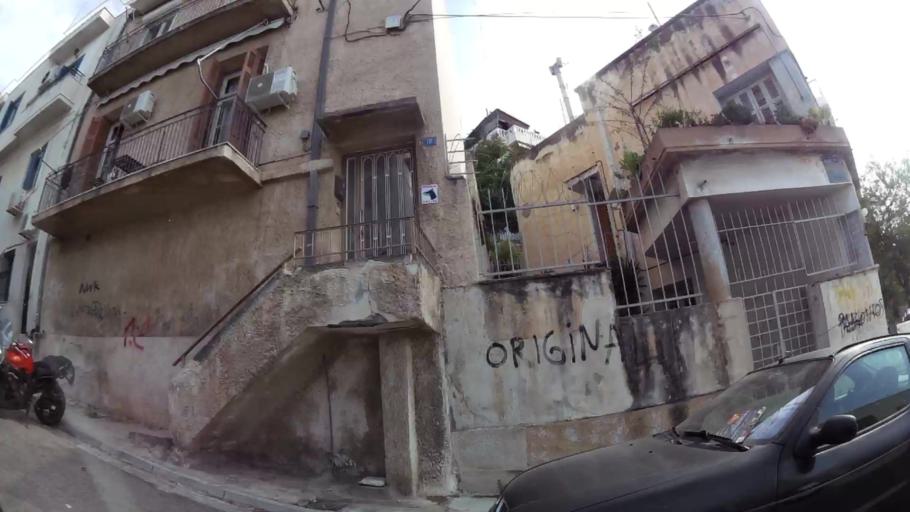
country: GR
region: Attica
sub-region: Nomarchia Athinas
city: Athens
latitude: 37.9651
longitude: 23.7162
